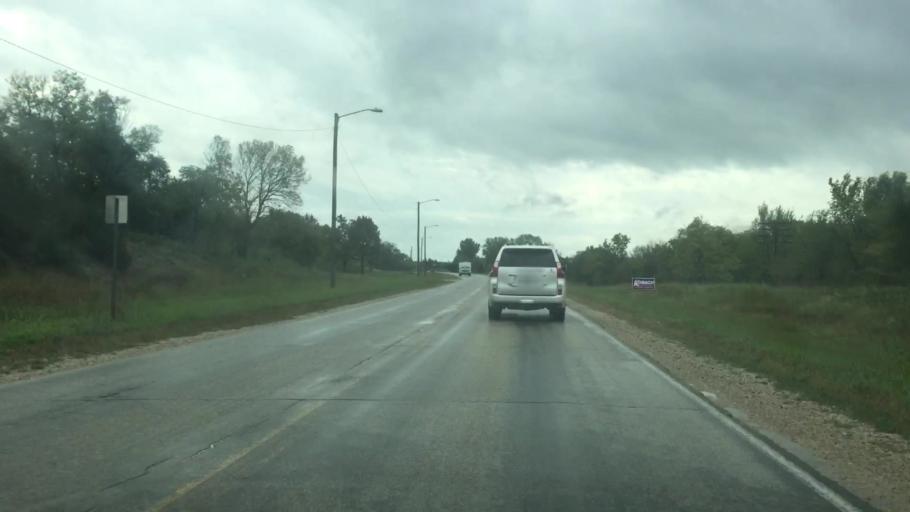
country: US
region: Kansas
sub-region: Allen County
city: Iola
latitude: 37.9069
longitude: -95.4098
